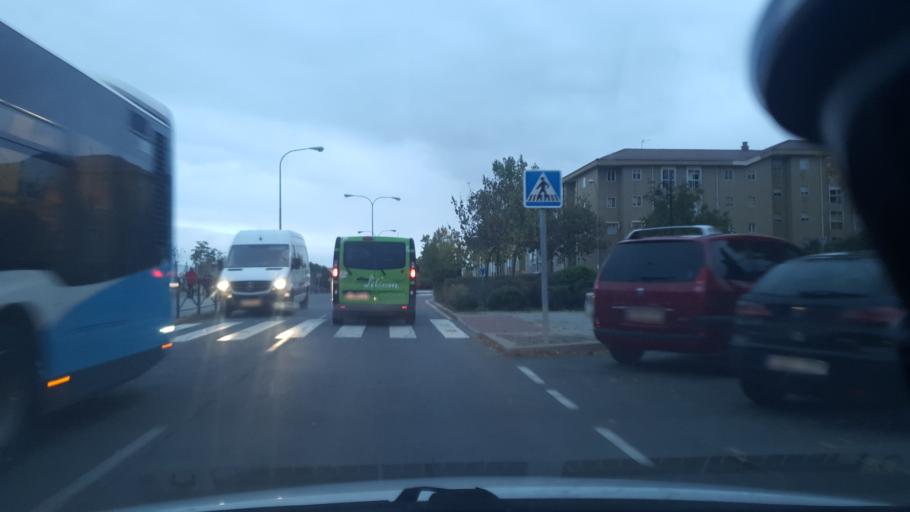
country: ES
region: Castille and Leon
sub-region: Provincia de Segovia
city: Segovia
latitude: 40.9323
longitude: -4.1027
